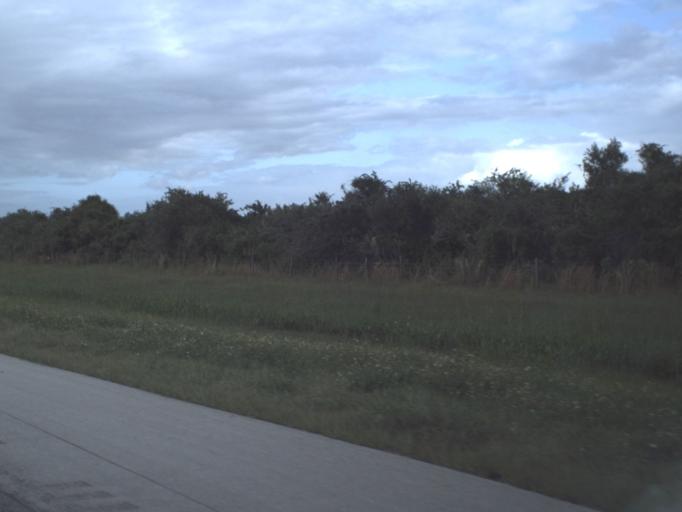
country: US
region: Florida
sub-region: Lee County
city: Suncoast Estates
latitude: 26.7588
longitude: -81.8718
